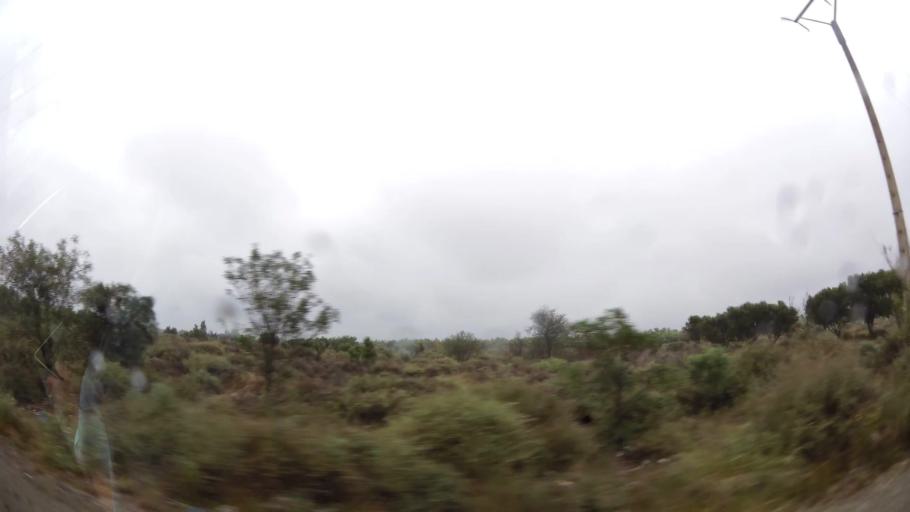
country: MA
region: Taza-Al Hoceima-Taounate
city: Imzourene
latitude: 35.1496
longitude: -3.8174
